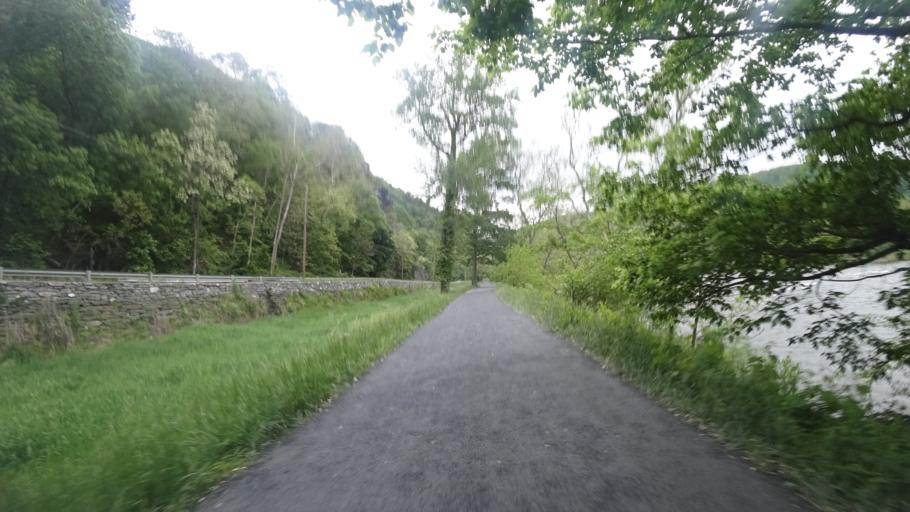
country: US
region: West Virginia
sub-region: Jefferson County
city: Bolivar
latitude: 39.3283
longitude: -77.7303
